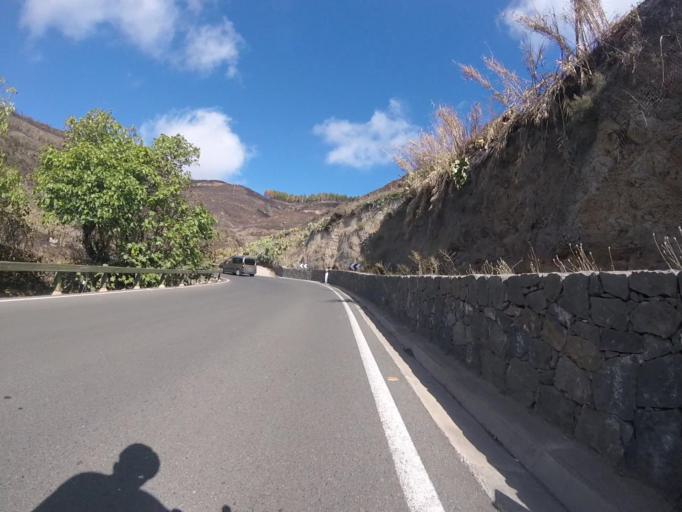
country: ES
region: Canary Islands
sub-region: Provincia de Las Palmas
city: Tejeda
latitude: 28.0088
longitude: -15.5935
